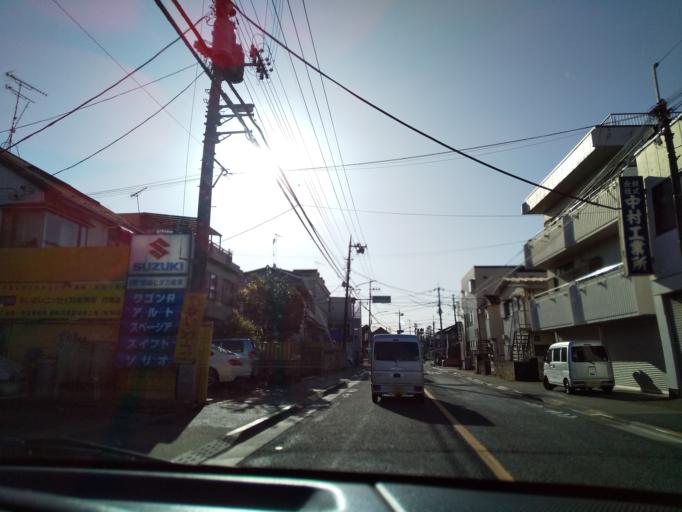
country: JP
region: Tokyo
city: Hino
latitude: 35.6996
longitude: 139.3872
